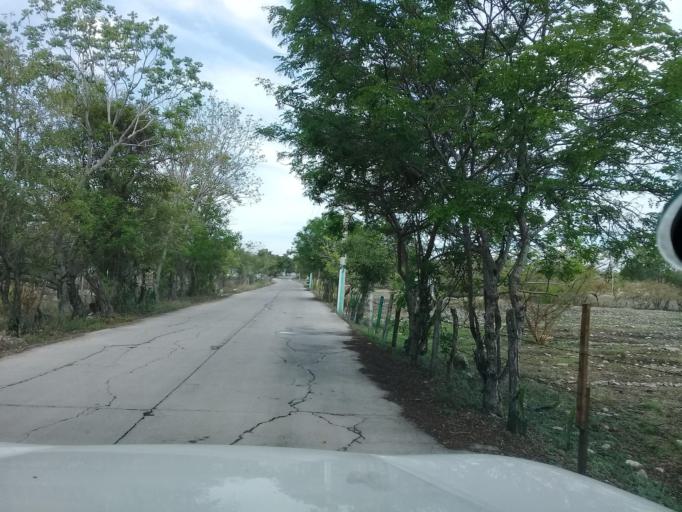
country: MX
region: Veracruz
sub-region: Emiliano Zapata
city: Plan del Rio
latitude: 19.3529
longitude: -96.6413
